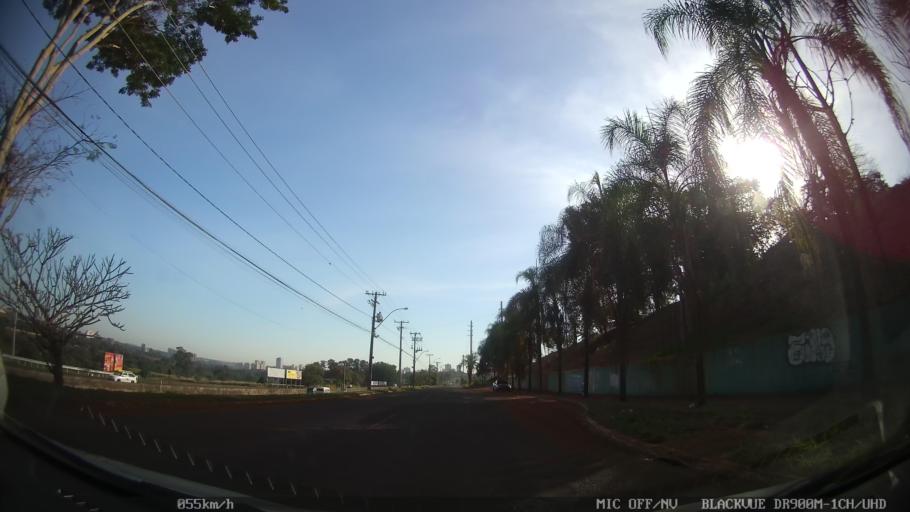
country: BR
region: Sao Paulo
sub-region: Ribeirao Preto
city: Ribeirao Preto
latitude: -21.2425
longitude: -47.8190
